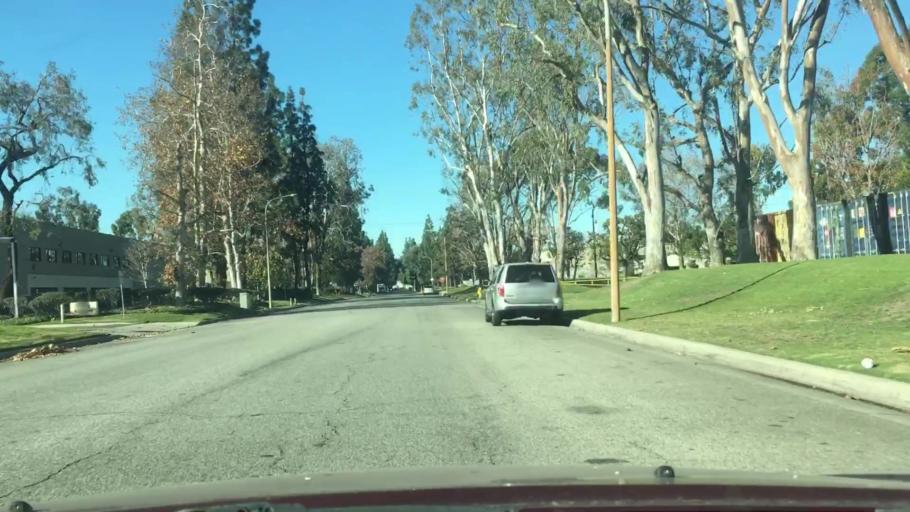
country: US
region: California
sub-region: Los Angeles County
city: Cerritos
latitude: 33.8824
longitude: -118.0536
